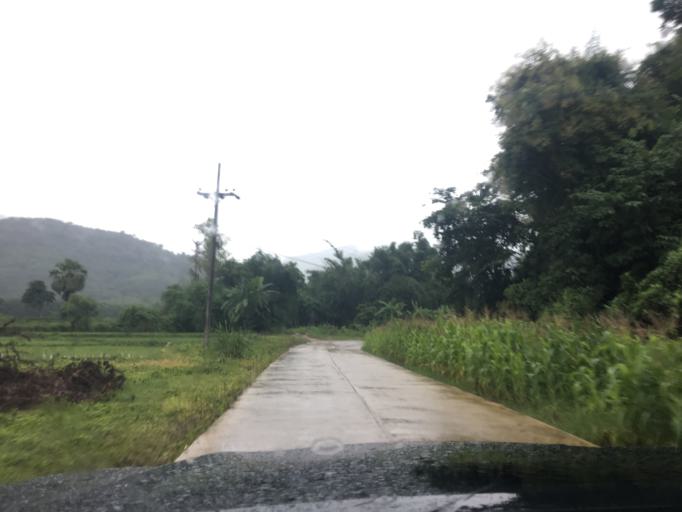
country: TH
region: Chiang Rai
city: Chiang Khong
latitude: 20.2964
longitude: 100.2571
